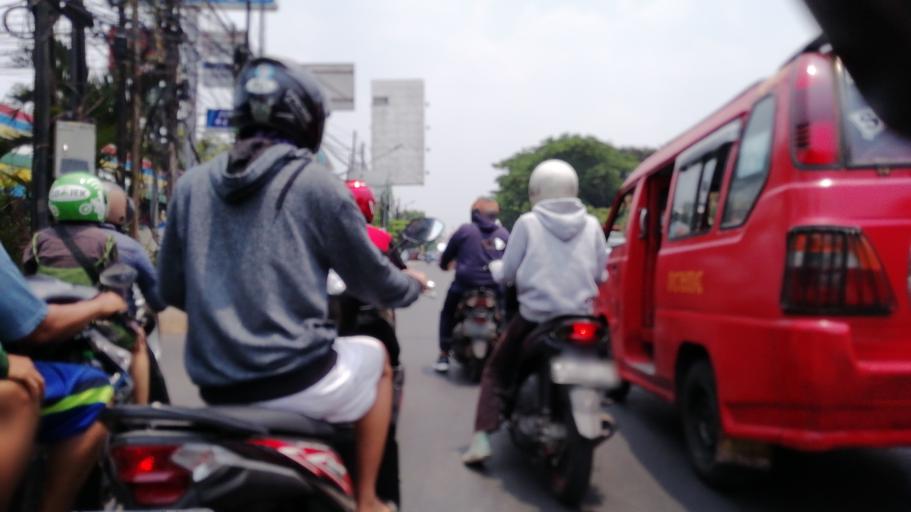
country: ID
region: West Java
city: Pamulang
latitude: -6.2966
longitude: 106.7950
